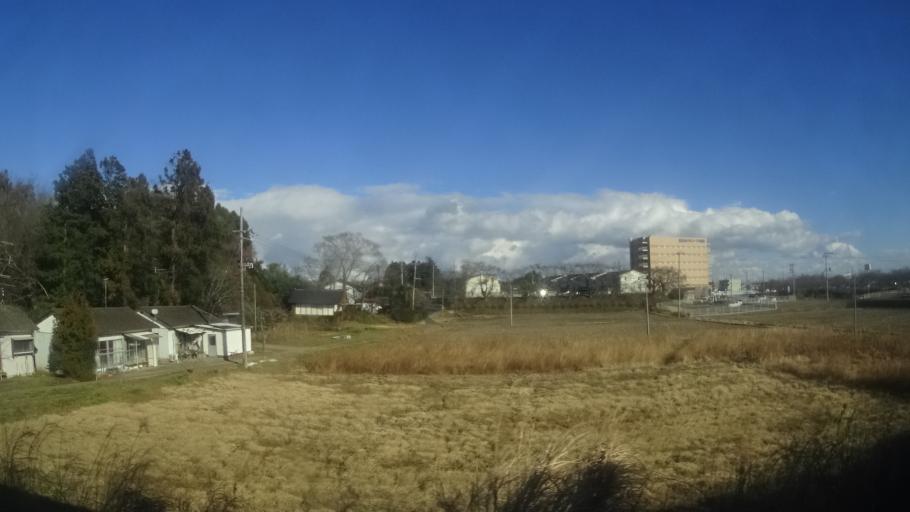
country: JP
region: Miyagi
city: Marumori
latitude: 37.8083
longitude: 140.9239
